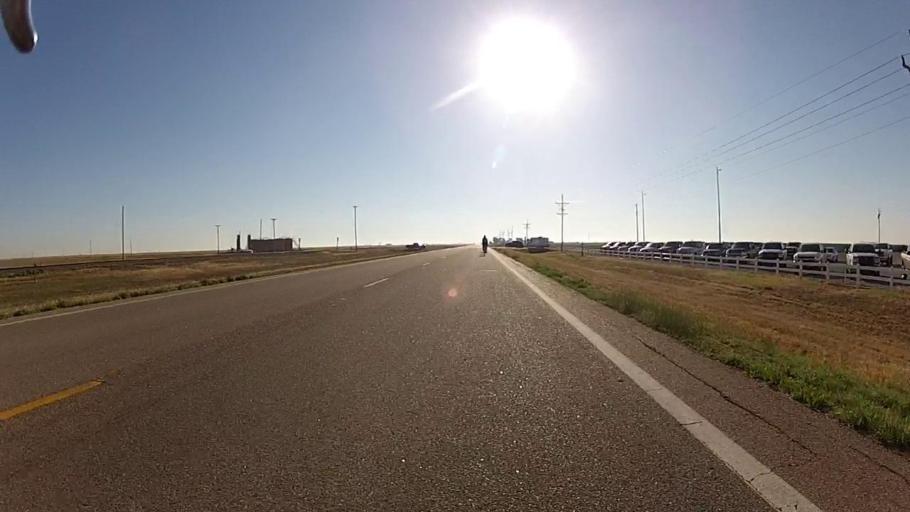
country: US
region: Kansas
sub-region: Haskell County
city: Sublette
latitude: 37.4957
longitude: -100.7995
